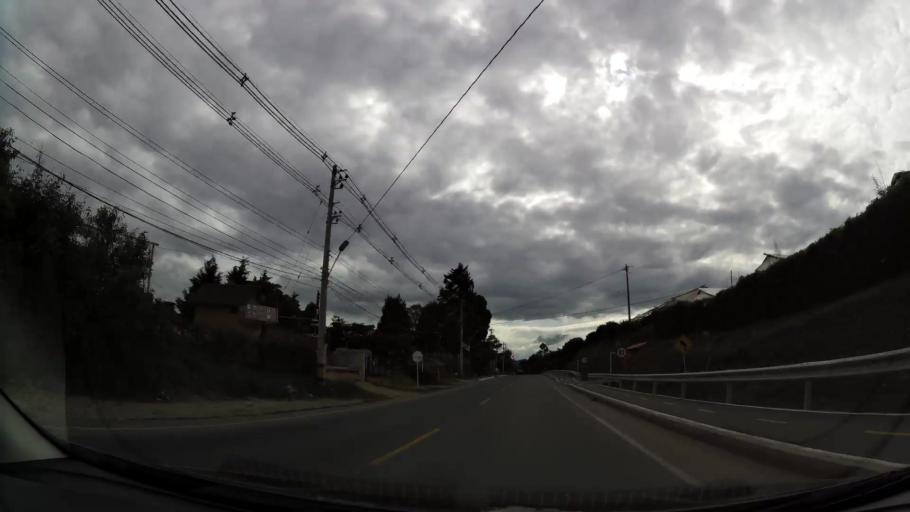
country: CO
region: Antioquia
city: Rionegro
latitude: 6.1515
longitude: -75.4150
